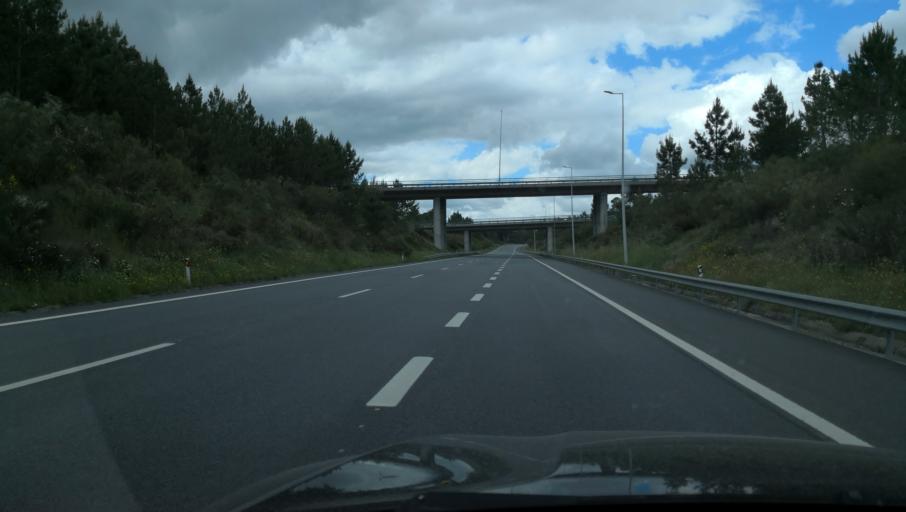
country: PT
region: Evora
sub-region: Vendas Novas
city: Vendas Novas
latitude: 38.6037
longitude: -8.6439
